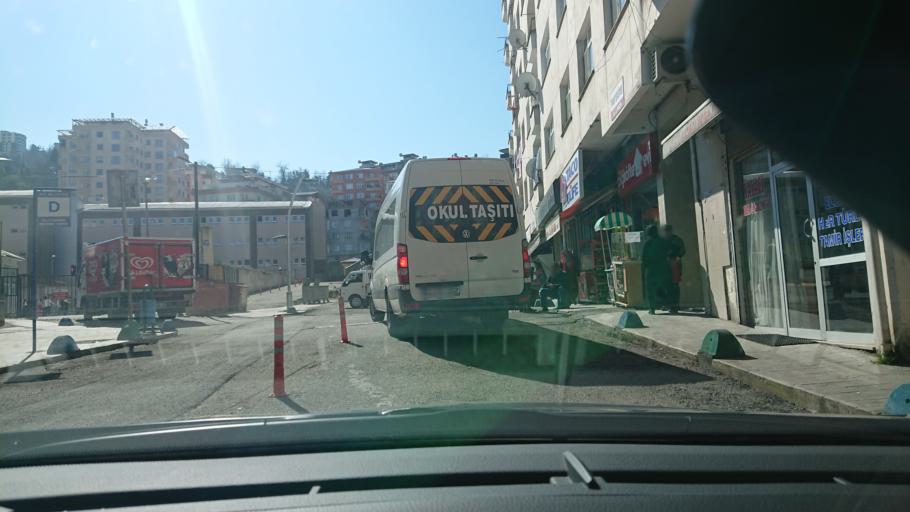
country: TR
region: Rize
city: Rize
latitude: 41.0223
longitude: 40.5284
